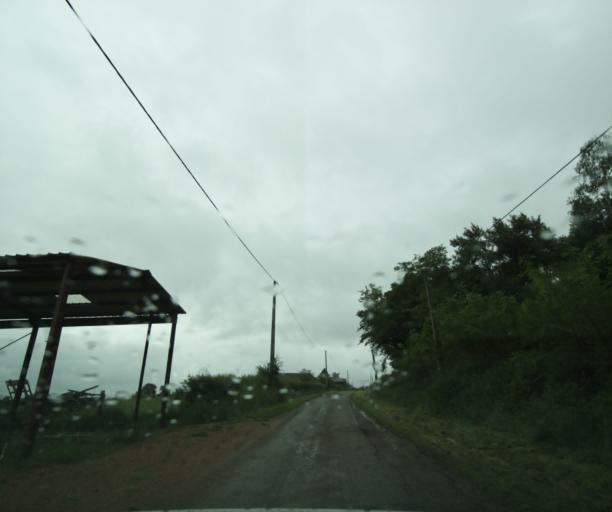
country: FR
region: Bourgogne
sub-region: Departement de Saone-et-Loire
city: Charolles
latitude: 46.4784
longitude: 4.2961
